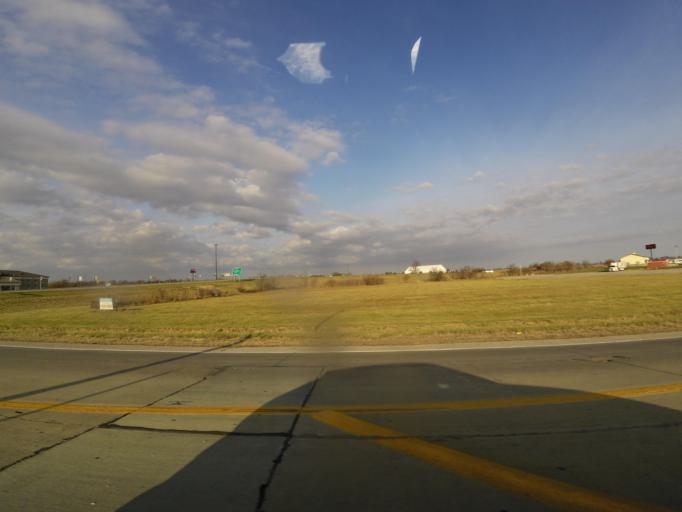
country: US
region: Illinois
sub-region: Fayette County
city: Vandalia
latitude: 38.9674
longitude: -89.1298
